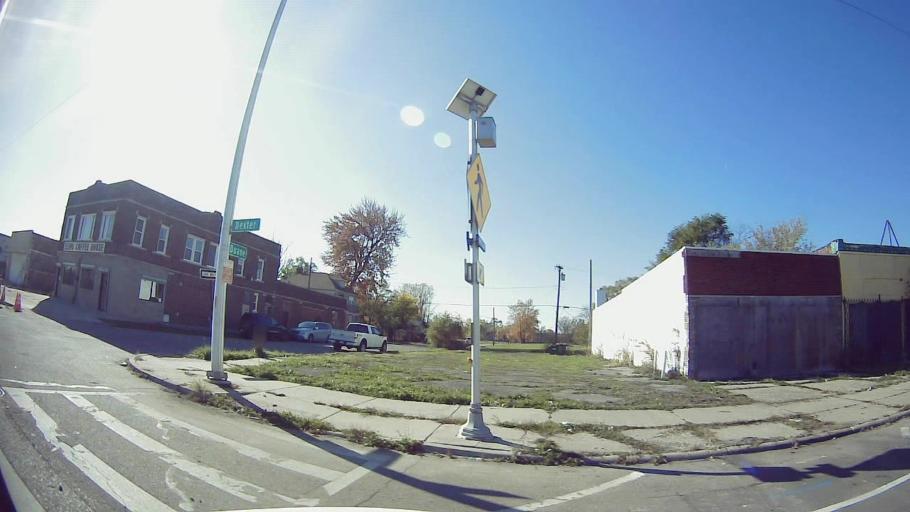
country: US
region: Michigan
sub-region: Wayne County
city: Highland Park
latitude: 42.3817
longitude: -83.1255
